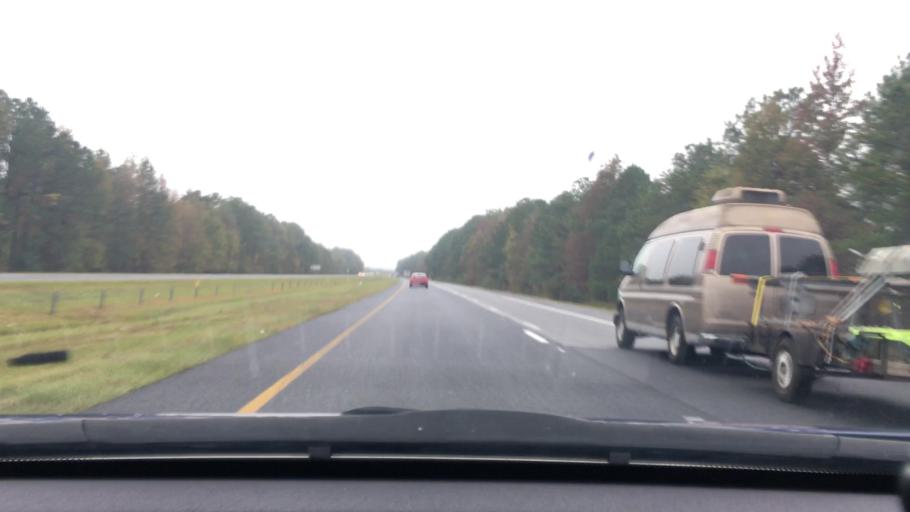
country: US
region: South Carolina
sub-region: Lee County
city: Bishopville
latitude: 34.1936
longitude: -80.1445
